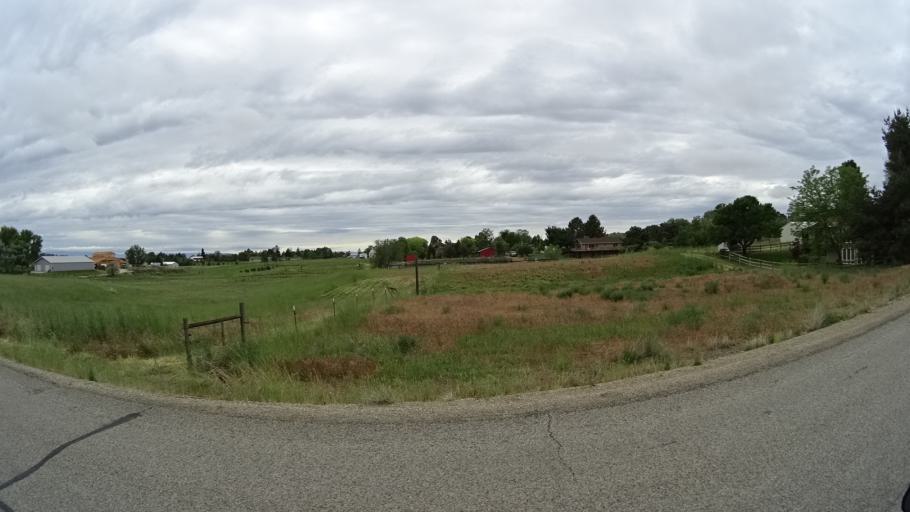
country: US
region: Idaho
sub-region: Ada County
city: Eagle
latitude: 43.7343
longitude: -116.3795
